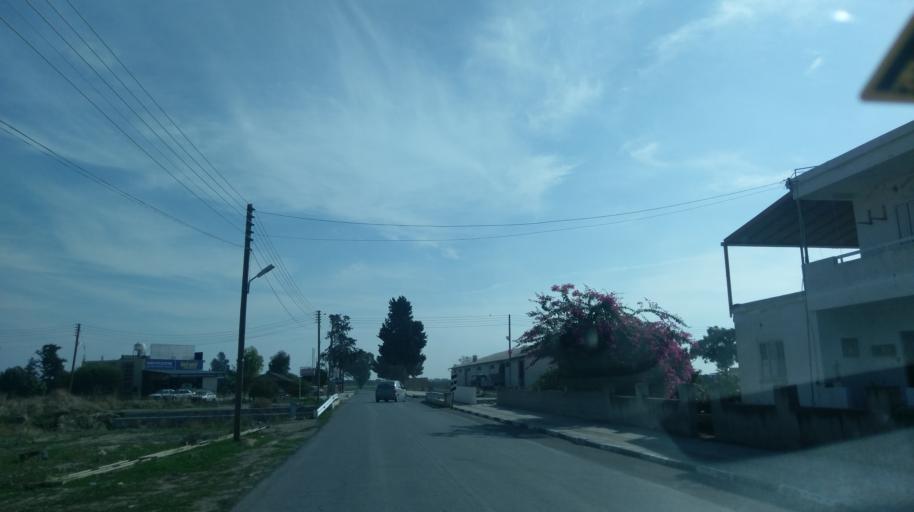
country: CY
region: Larnaka
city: Pergamos
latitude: 35.1069
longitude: 33.6909
